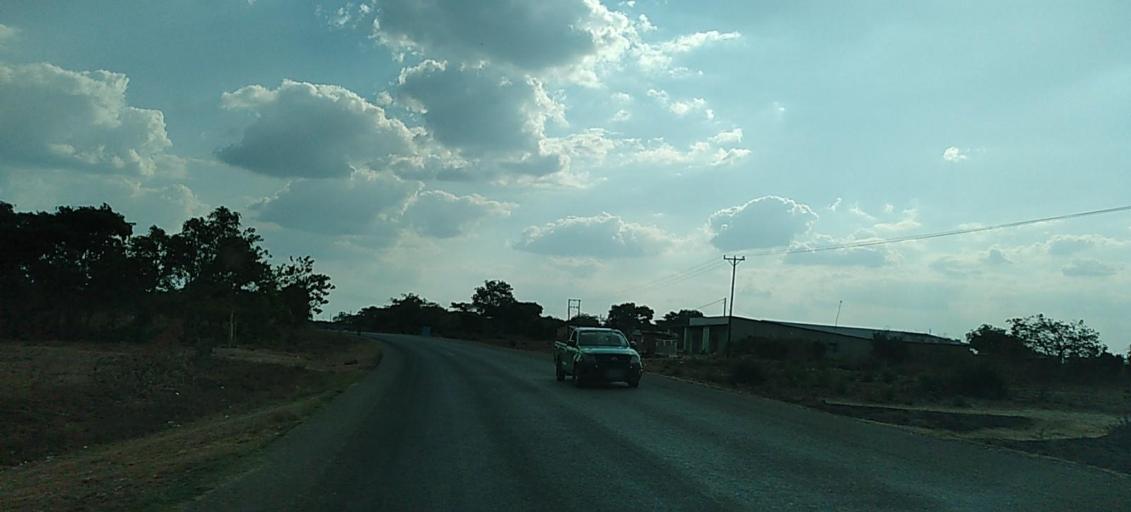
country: ZM
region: Copperbelt
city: Luanshya
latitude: -13.3644
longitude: 28.4079
